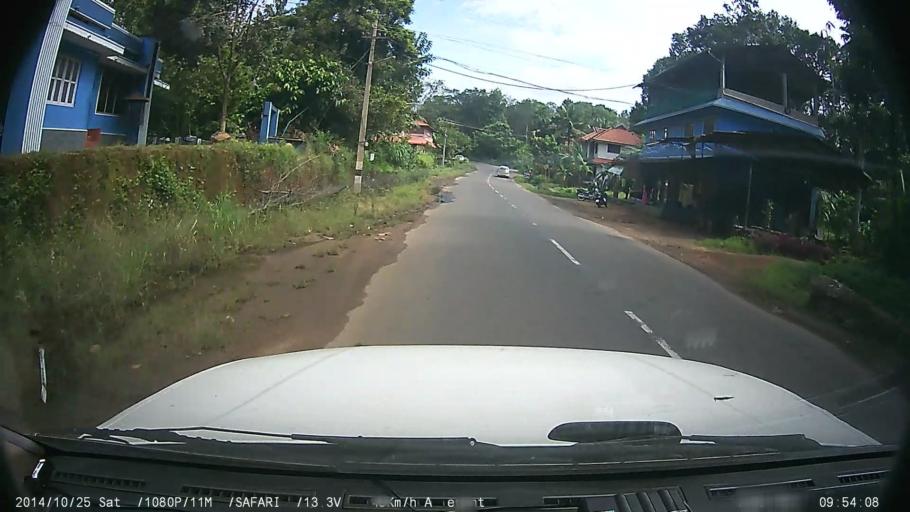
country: IN
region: Kerala
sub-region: Kottayam
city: Palackattumala
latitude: 9.7873
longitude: 76.5792
